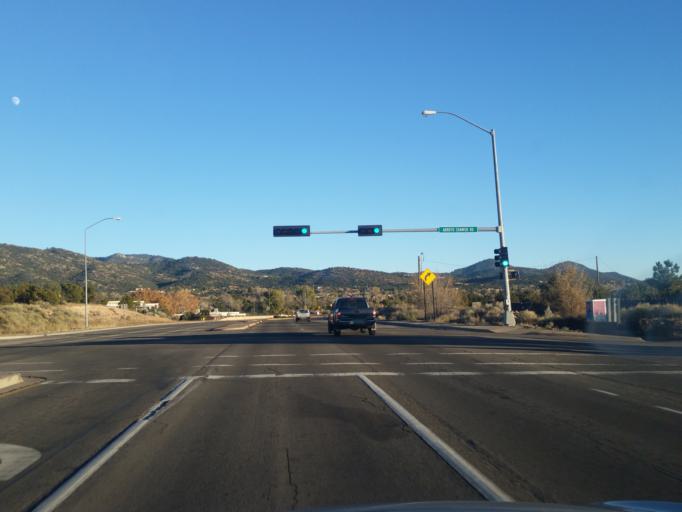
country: US
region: New Mexico
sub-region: Santa Fe County
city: Santa Fe
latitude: 35.6559
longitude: -105.9418
